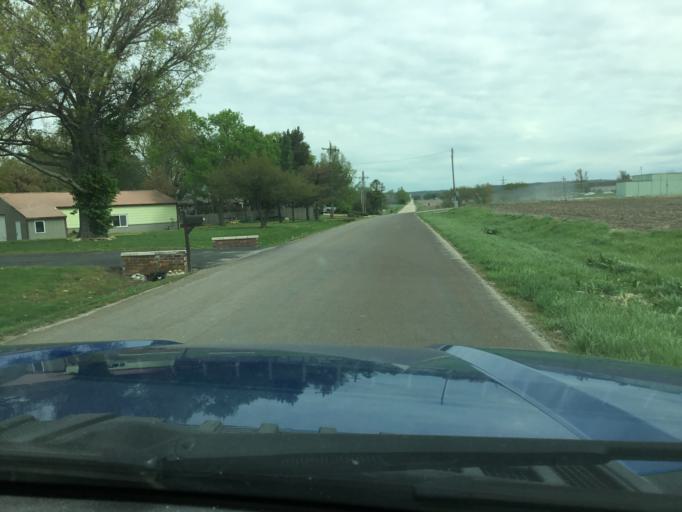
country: US
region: Kansas
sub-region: Douglas County
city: Lawrence
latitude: 39.0033
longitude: -95.2241
